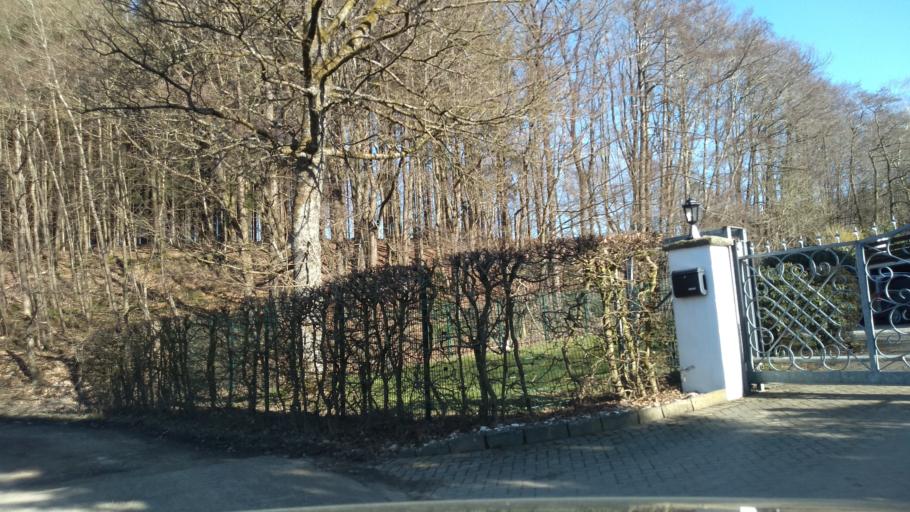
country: DE
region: North Rhine-Westphalia
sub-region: Regierungsbezirk Arnsberg
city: Herscheid
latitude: 51.1700
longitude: 7.7078
